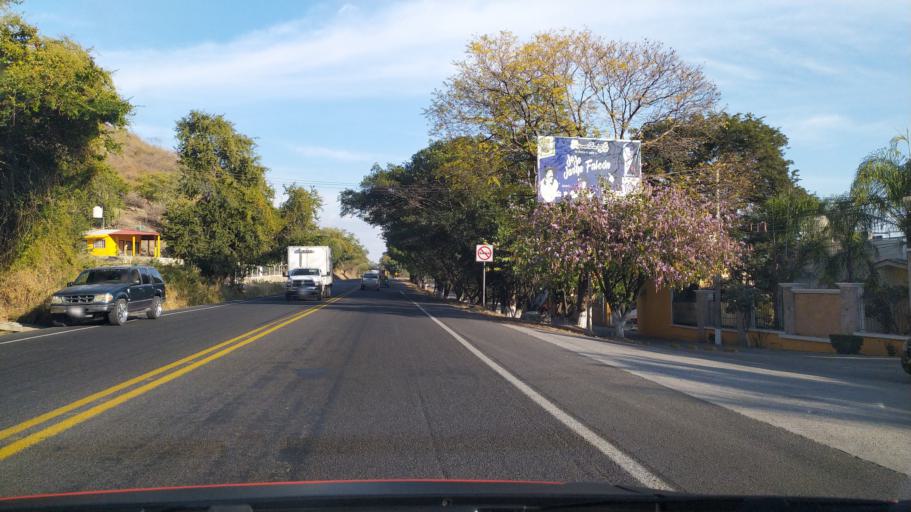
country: MX
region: Jalisco
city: Jamay
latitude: 20.2939
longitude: -102.7334
